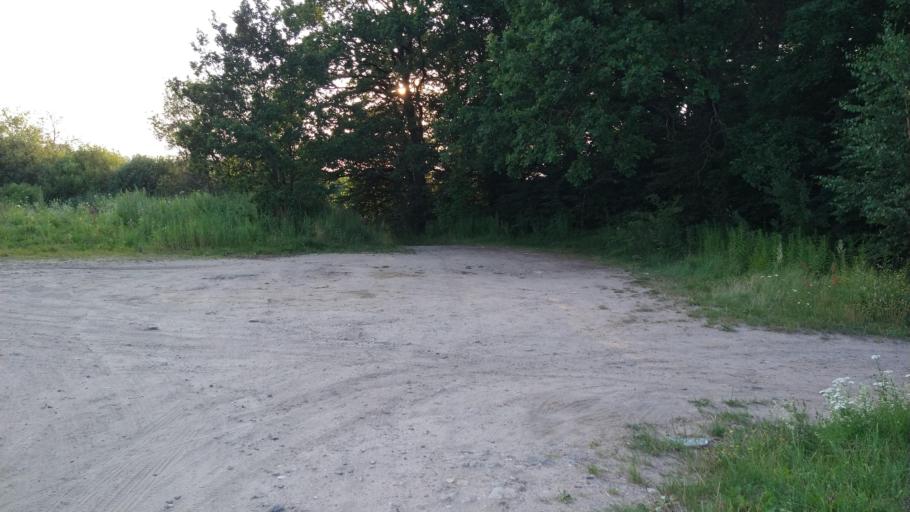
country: PL
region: Warmian-Masurian Voivodeship
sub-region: Powiat olsztynski
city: Olsztyn
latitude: 53.7846
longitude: 20.5507
